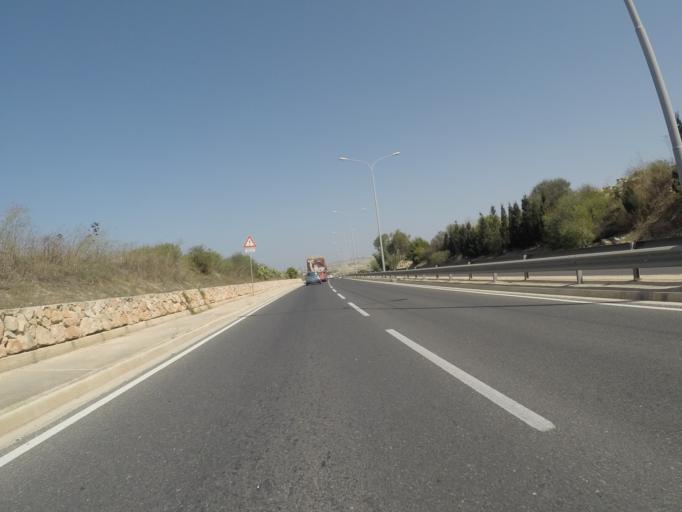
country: MT
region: Saint Paul's Bay
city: San Pawl il-Bahar
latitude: 35.9460
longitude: 14.4049
